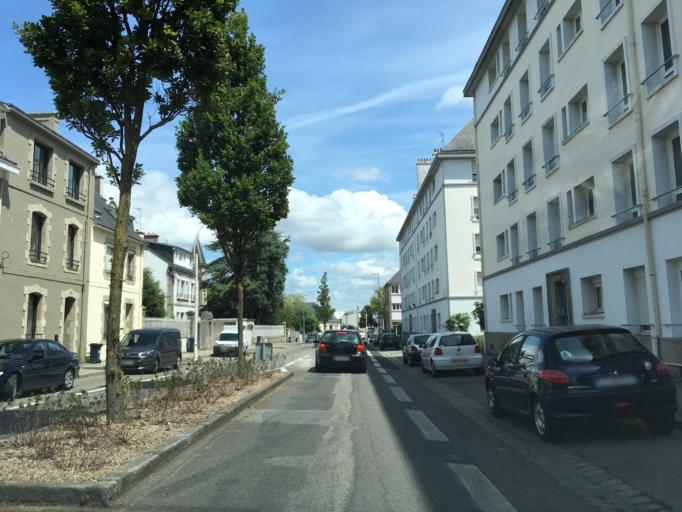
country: FR
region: Brittany
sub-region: Departement du Morbihan
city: Lorient
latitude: 47.7422
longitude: -3.3704
